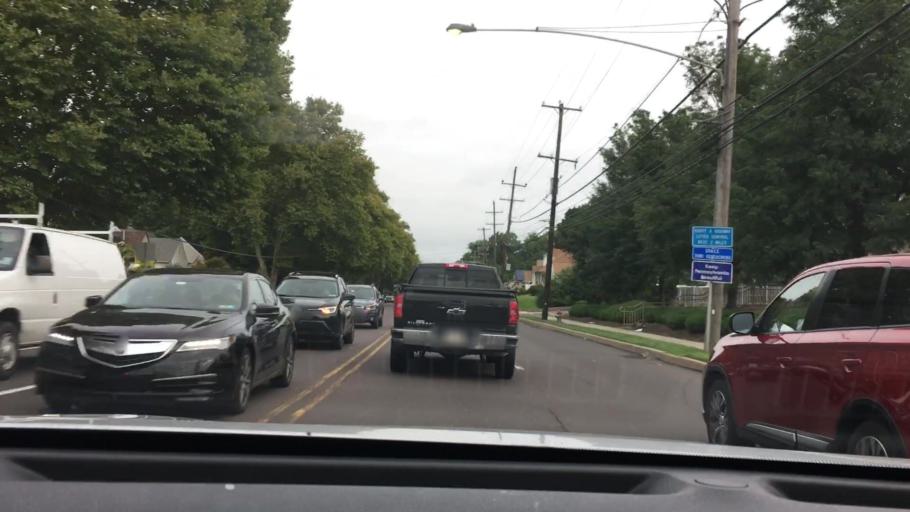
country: US
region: Pennsylvania
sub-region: Montgomery County
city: Hatboro
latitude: 40.1904
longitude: -75.1037
